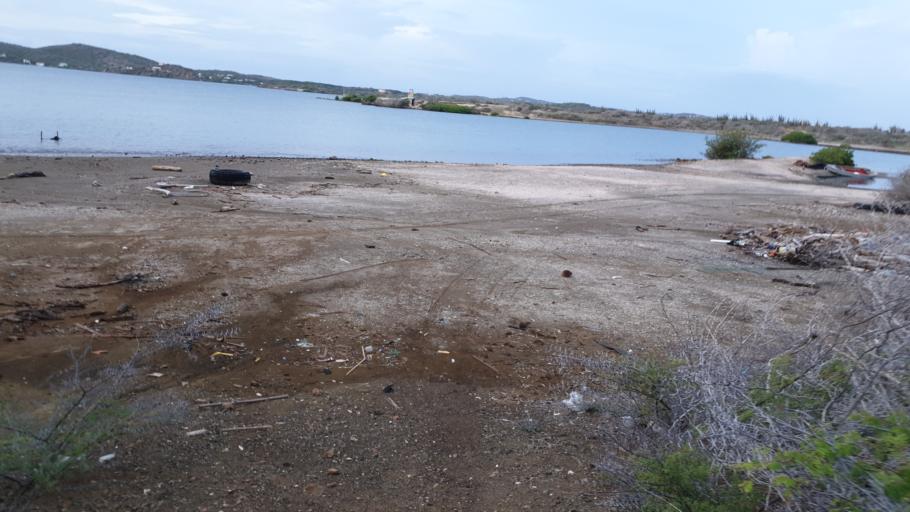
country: CW
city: Newport
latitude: 12.1269
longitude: -68.8151
